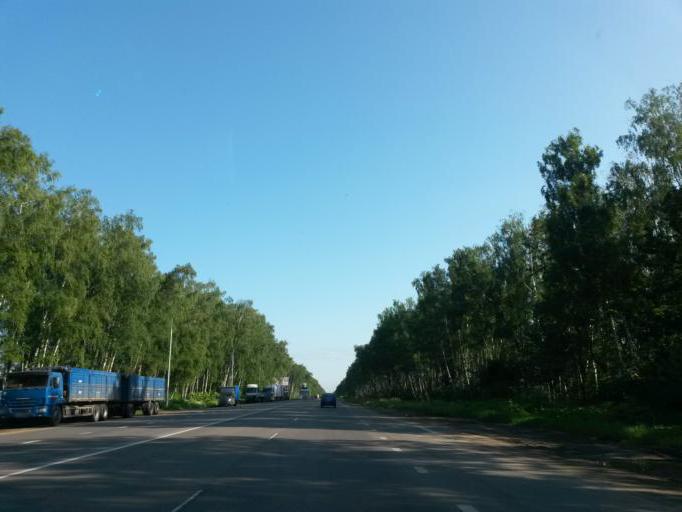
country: RU
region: Moskovskaya
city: Belyye Stolby
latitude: 55.2790
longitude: 37.8245
